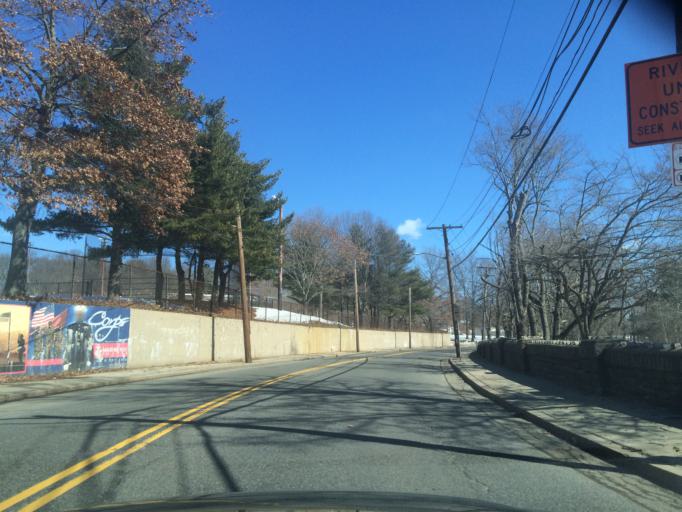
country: US
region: Massachusetts
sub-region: Norfolk County
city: Dedham
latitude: 42.2466
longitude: -71.1362
